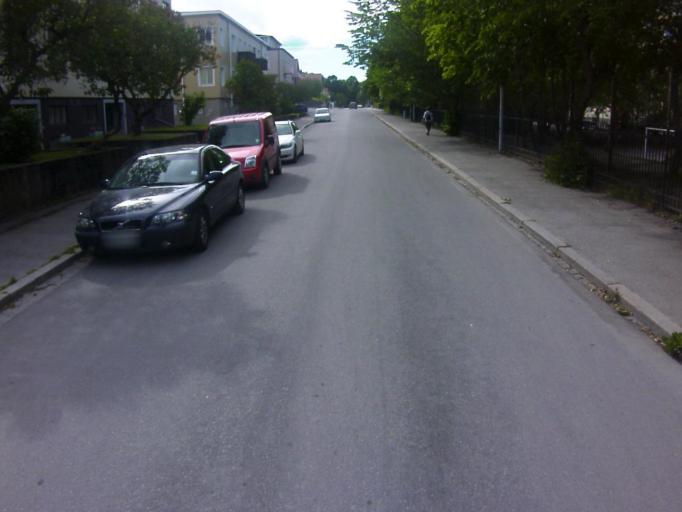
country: SE
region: Soedermanland
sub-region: Eskilstuna Kommun
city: Eskilstuna
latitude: 59.3644
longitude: 16.5073
